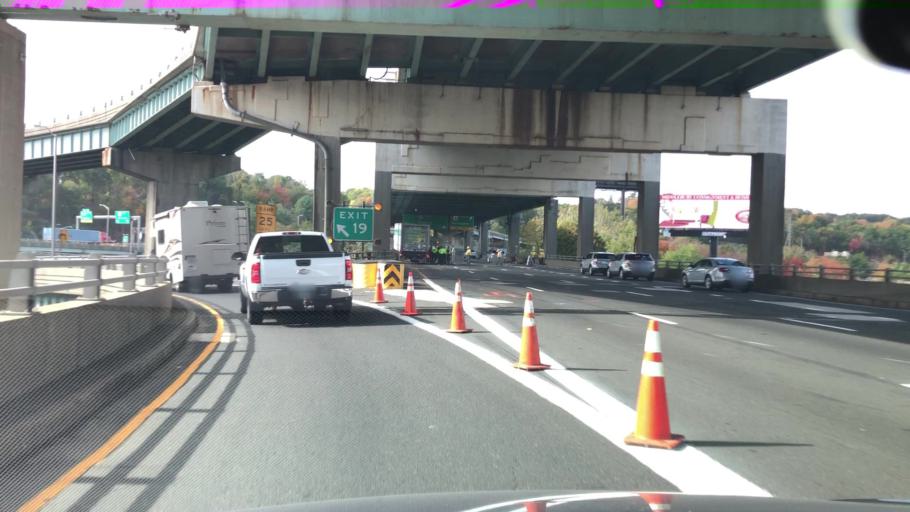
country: US
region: Connecticut
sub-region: New Haven County
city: Waterbury
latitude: 41.5517
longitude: -73.0483
